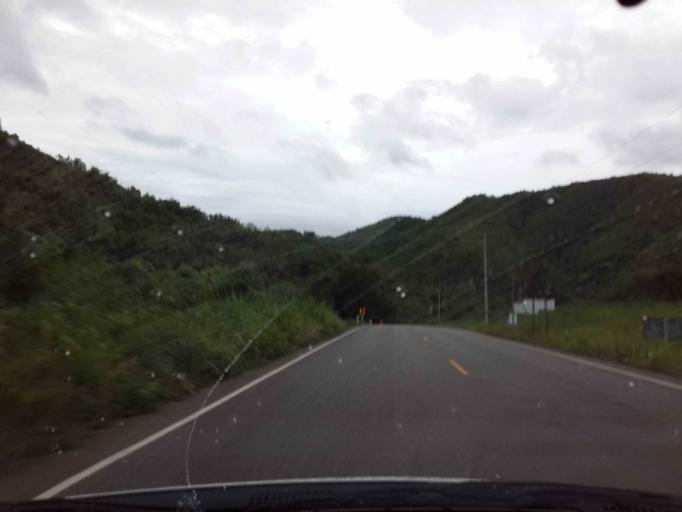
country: TH
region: Ratchaburi
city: Suan Phueng
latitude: 13.5756
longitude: 99.2522
